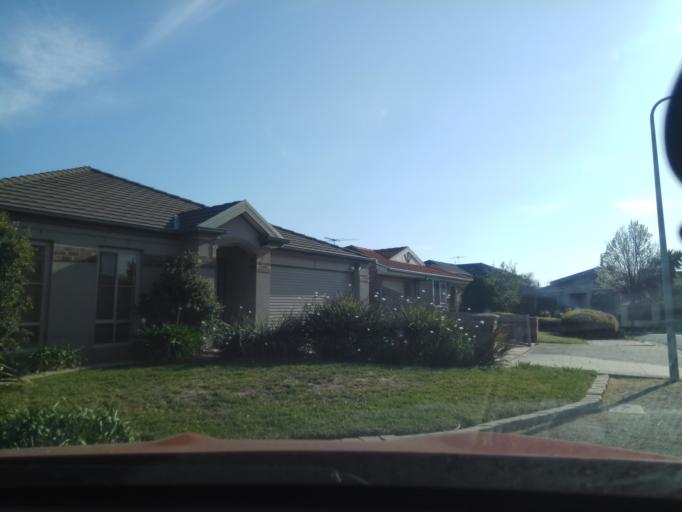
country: AU
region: Victoria
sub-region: Hobsons Bay
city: Altona Meadows
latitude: -37.8815
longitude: 144.7722
